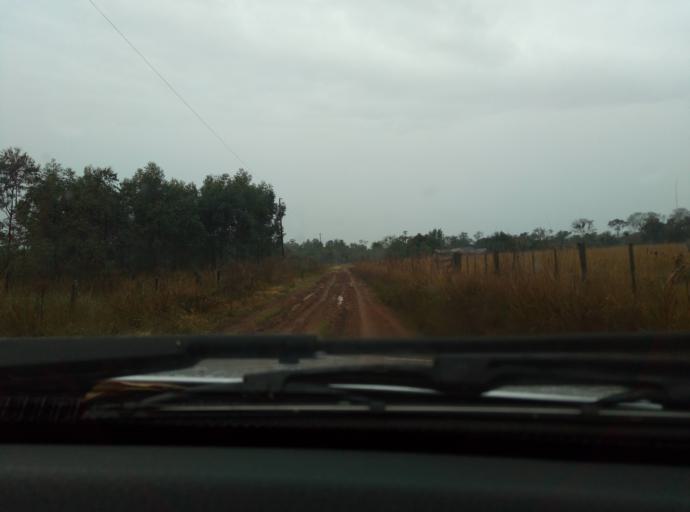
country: PY
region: Caaguazu
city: Carayao
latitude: -25.1040
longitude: -56.4168
